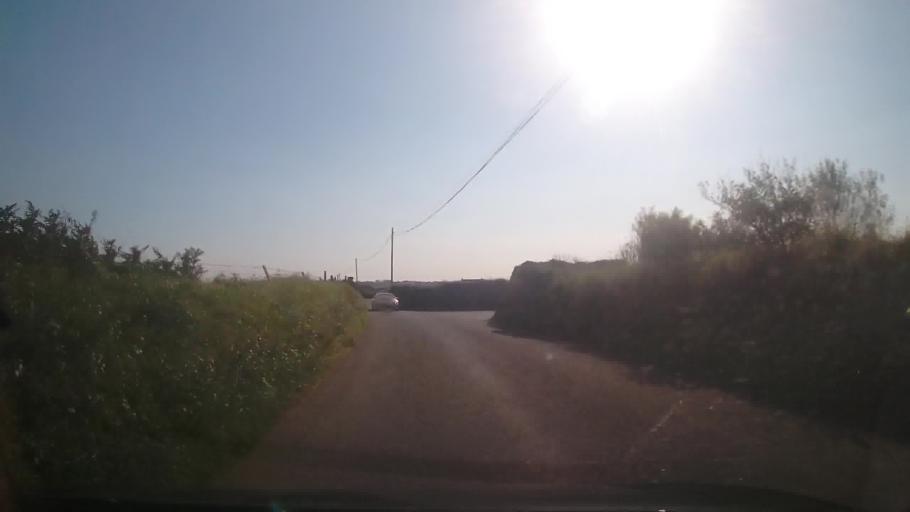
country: GB
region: Wales
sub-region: Pembrokeshire
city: Saint David's
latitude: 51.9039
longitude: -5.2447
